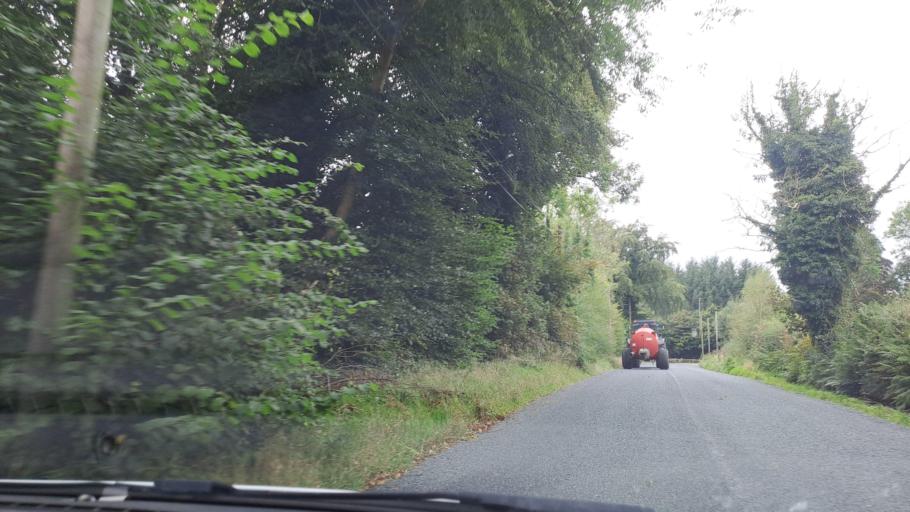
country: IE
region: Ulster
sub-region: An Cabhan
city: Bailieborough
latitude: 53.9948
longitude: -6.9143
